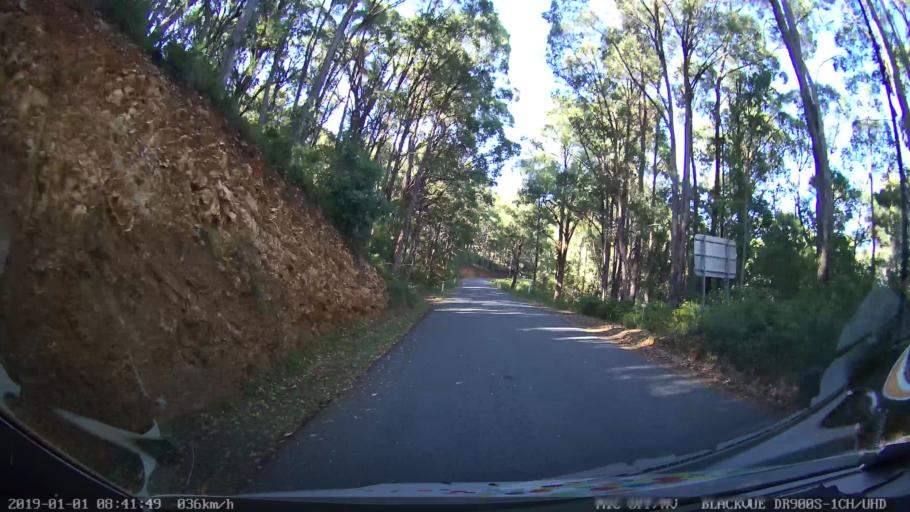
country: AU
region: New South Wales
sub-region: Snowy River
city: Jindabyne
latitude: -36.3224
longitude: 148.1978
